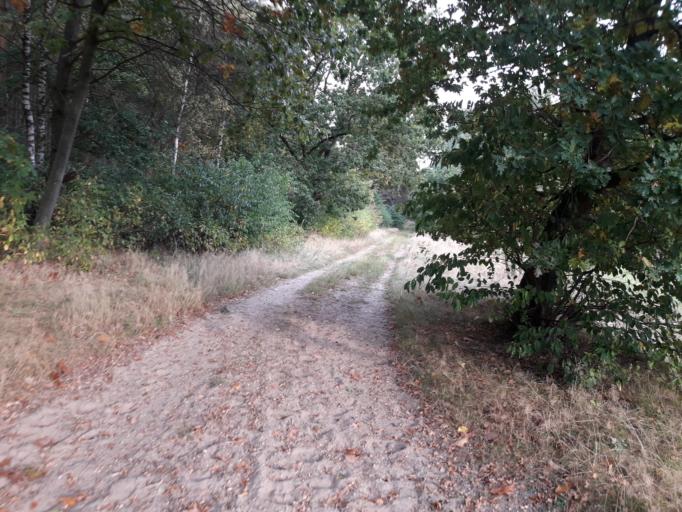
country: DE
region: Schleswig-Holstein
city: Wiershop
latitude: 53.4297
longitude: 10.4326
